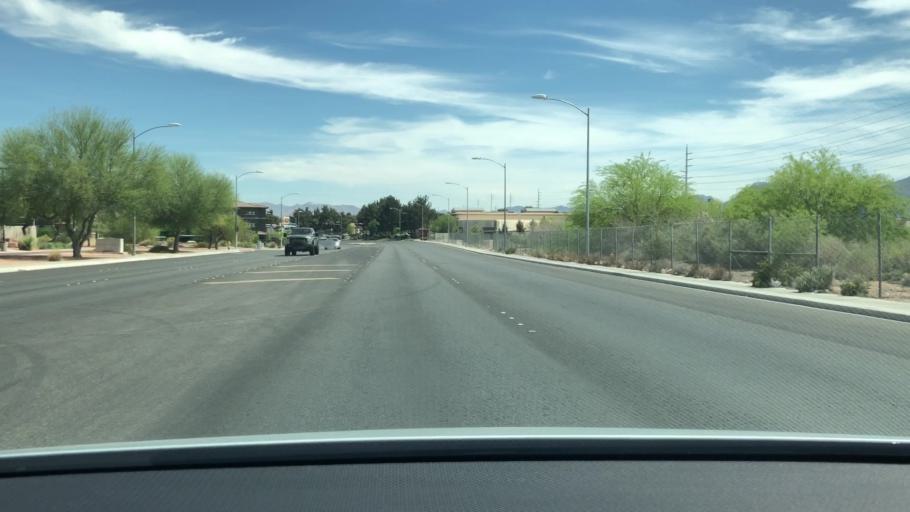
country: US
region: Nevada
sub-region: Clark County
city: Whitney
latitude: 36.0837
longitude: -115.0570
